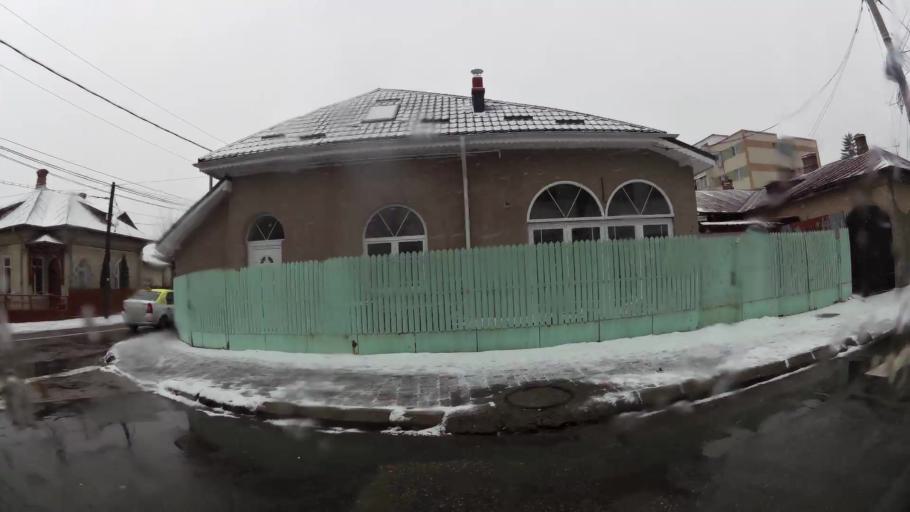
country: RO
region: Dambovita
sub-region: Municipiul Targoviste
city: Targoviste
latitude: 44.9285
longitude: 25.4513
